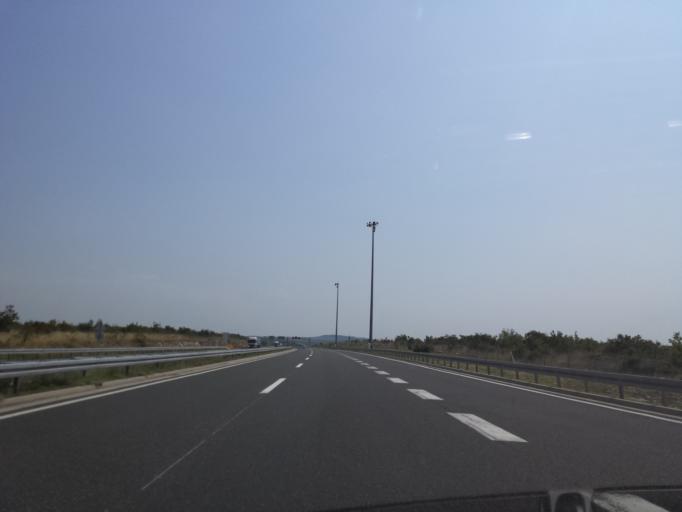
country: HR
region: Zadarska
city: Galovac
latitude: 44.1133
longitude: 15.4463
